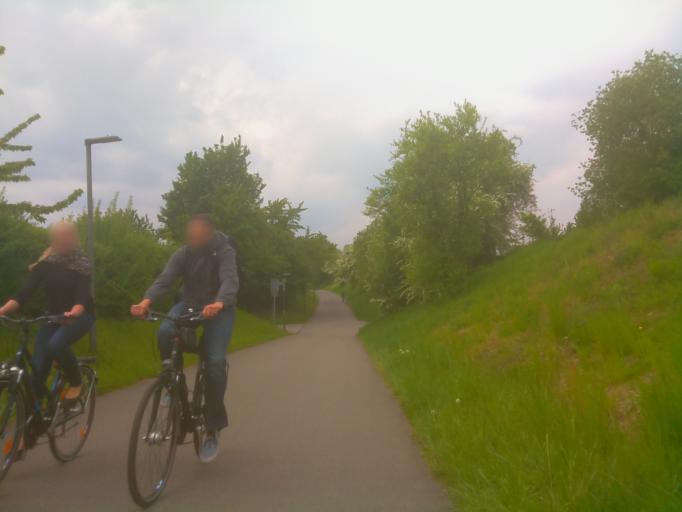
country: DE
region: Baden-Wuerttemberg
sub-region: Karlsruhe Region
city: Heidelberg
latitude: 49.3934
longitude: 8.6809
